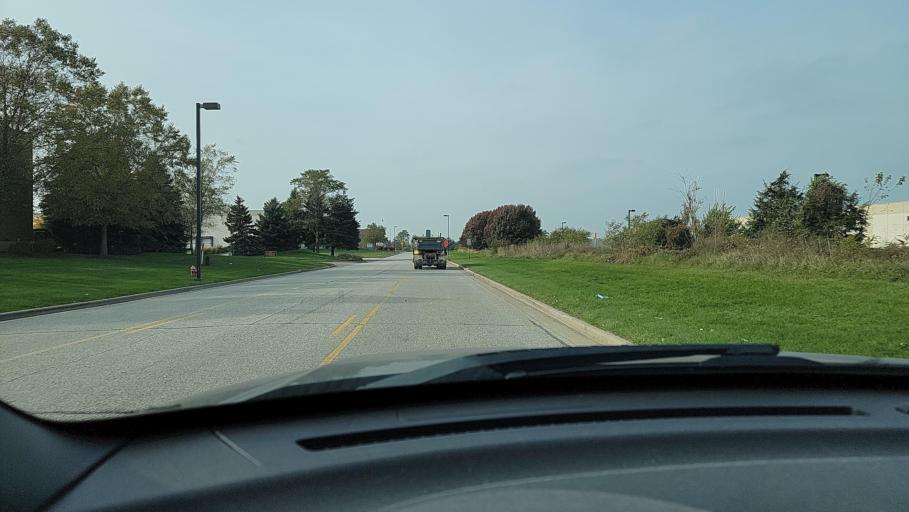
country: US
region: Indiana
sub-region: Porter County
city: Portage
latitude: 41.6049
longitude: -87.1612
